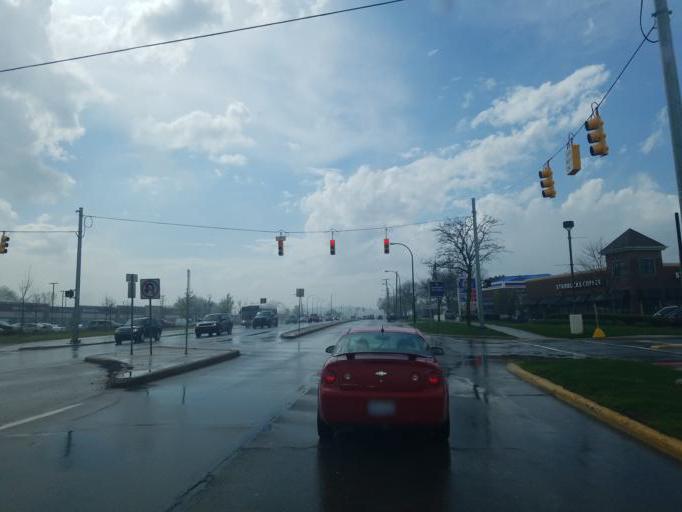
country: US
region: Michigan
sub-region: Washtenaw County
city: Ann Arbor
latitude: 42.2553
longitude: -83.6874
